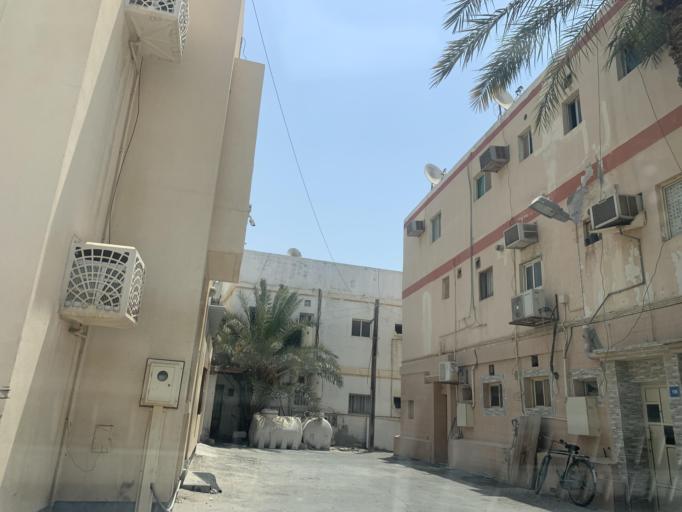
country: BH
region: Manama
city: Jidd Hafs
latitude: 26.2099
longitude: 50.4747
